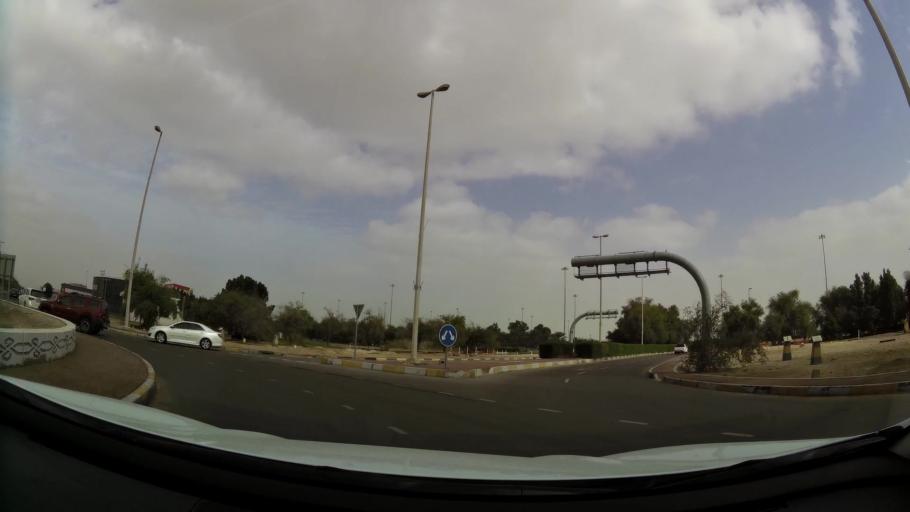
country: AE
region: Abu Dhabi
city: Abu Dhabi
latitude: 24.4117
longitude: 54.5069
